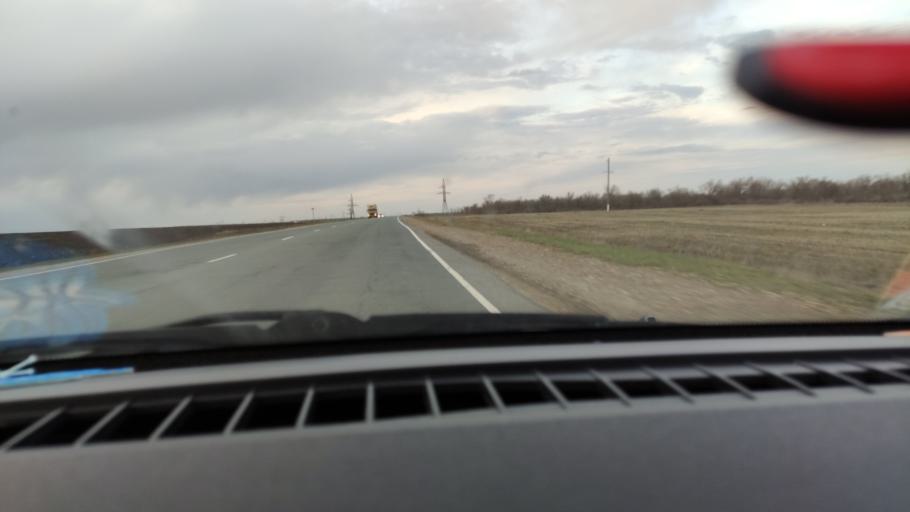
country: RU
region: Saratov
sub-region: Saratovskiy Rayon
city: Saratov
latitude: 51.7473
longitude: 46.0554
